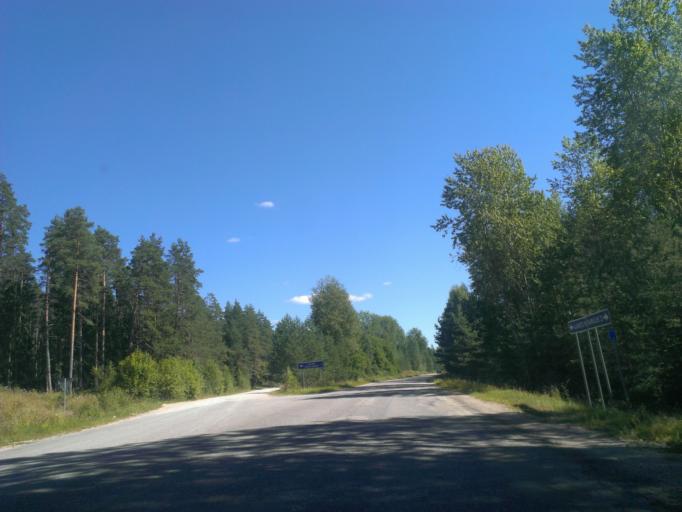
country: LV
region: Incukalns
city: Incukalns
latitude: 57.0295
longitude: 24.7319
